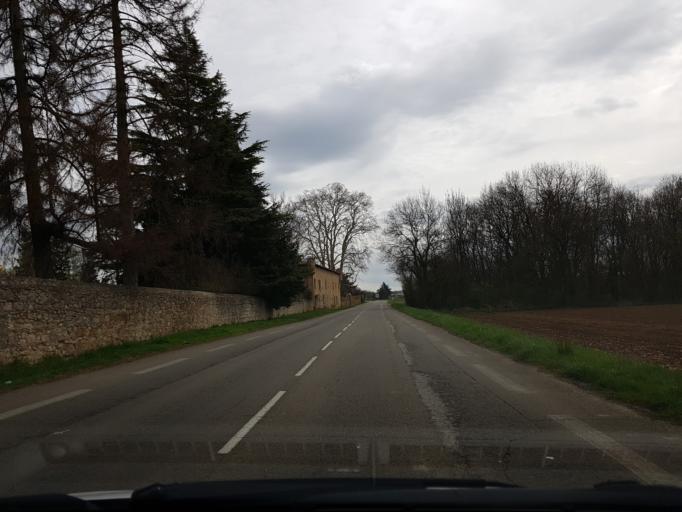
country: FR
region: Rhone-Alpes
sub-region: Departement de l'Ain
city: Trevoux
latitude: 45.9432
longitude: 4.7482
